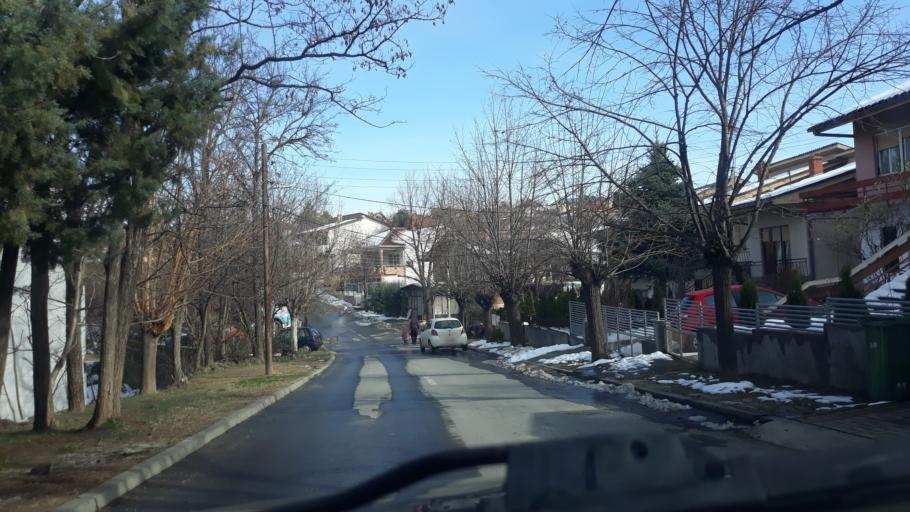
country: MK
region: Negotino
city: Negotino
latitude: 41.4810
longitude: 22.0837
